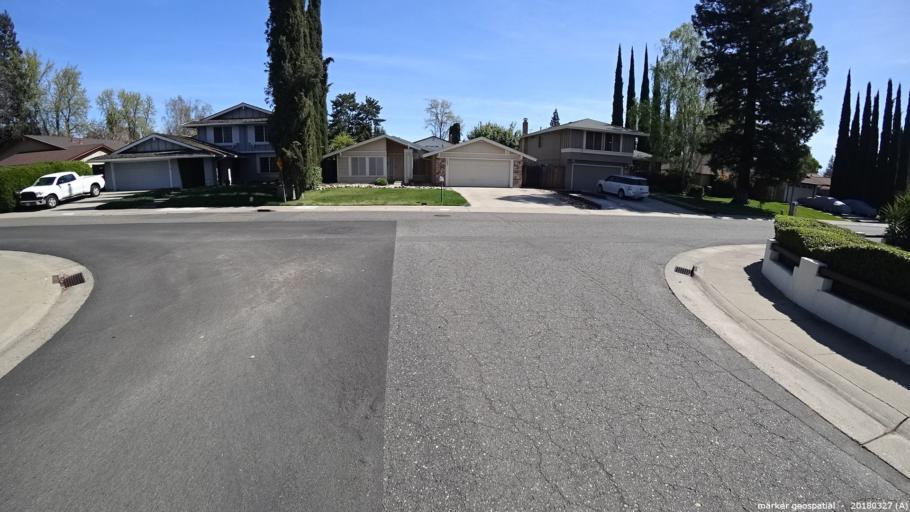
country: US
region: California
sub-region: Sacramento County
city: La Riviera
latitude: 38.5596
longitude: -121.3561
